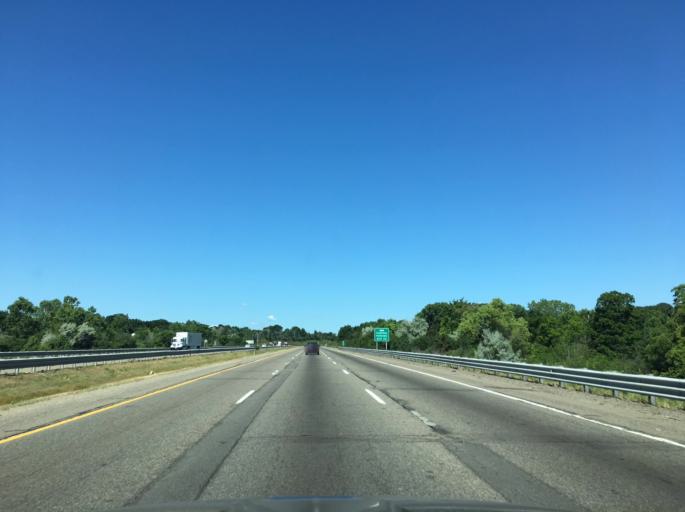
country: US
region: Michigan
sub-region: Oakland County
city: Troy
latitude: 42.6049
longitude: -83.1899
